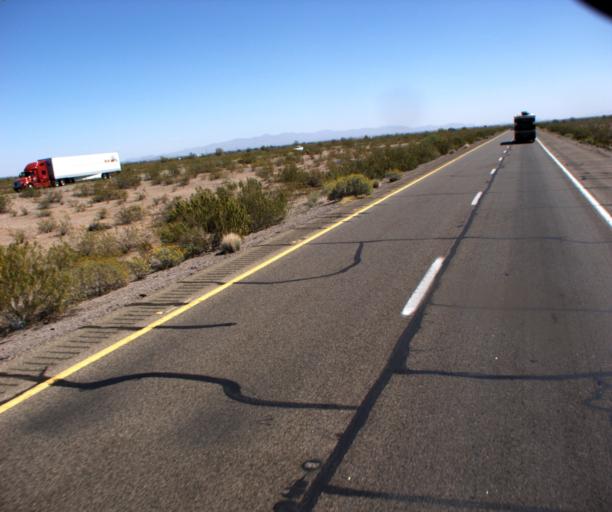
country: US
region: Arizona
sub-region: Maricopa County
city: Buckeye
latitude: 33.5061
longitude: -112.9857
